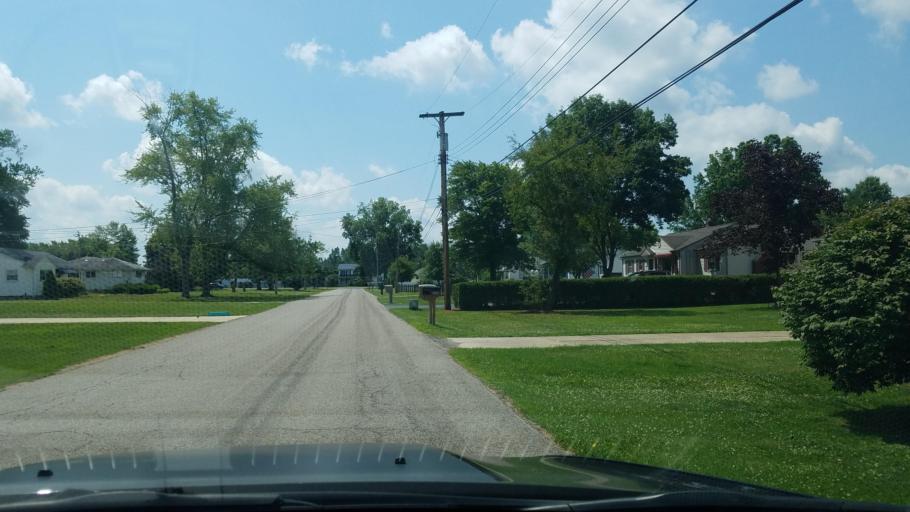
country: US
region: Ohio
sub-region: Trumbull County
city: Champion Heights
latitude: 41.3103
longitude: -80.8570
